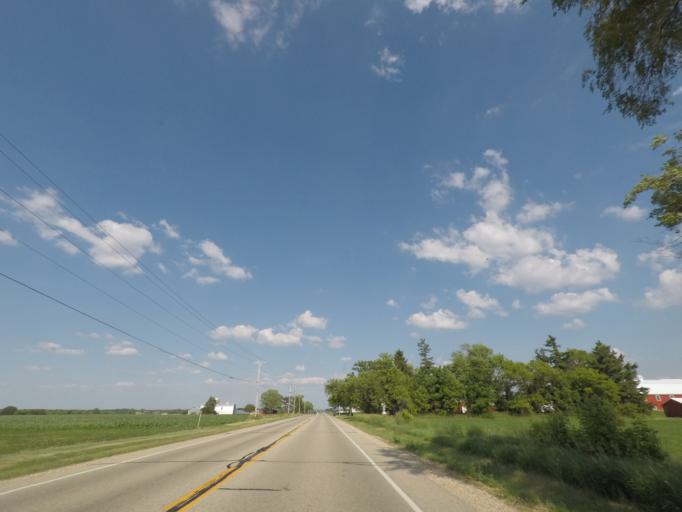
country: US
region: Wisconsin
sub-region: Walworth County
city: East Troy
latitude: 42.7927
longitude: -88.4565
